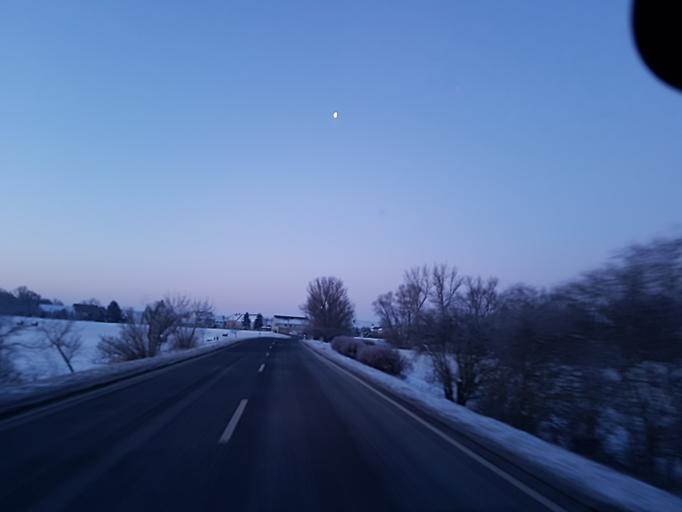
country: DE
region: Brandenburg
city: Muhlberg
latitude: 51.4235
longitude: 13.1841
